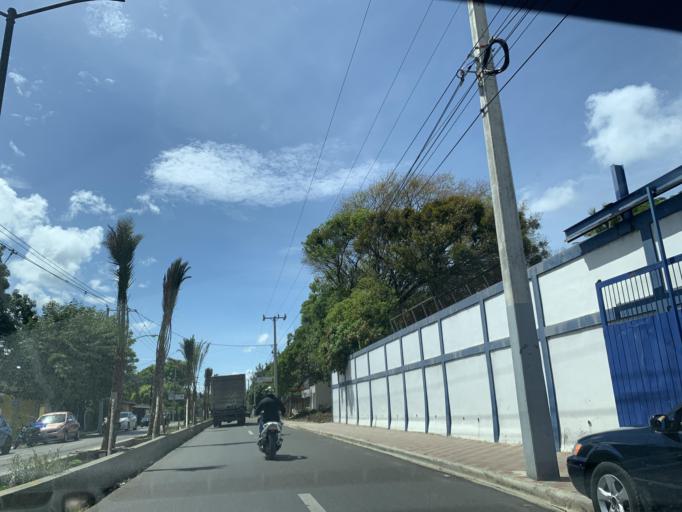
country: DO
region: Puerto Plata
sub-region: Puerto Plata
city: Puerto Plata
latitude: 19.7900
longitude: -70.6795
